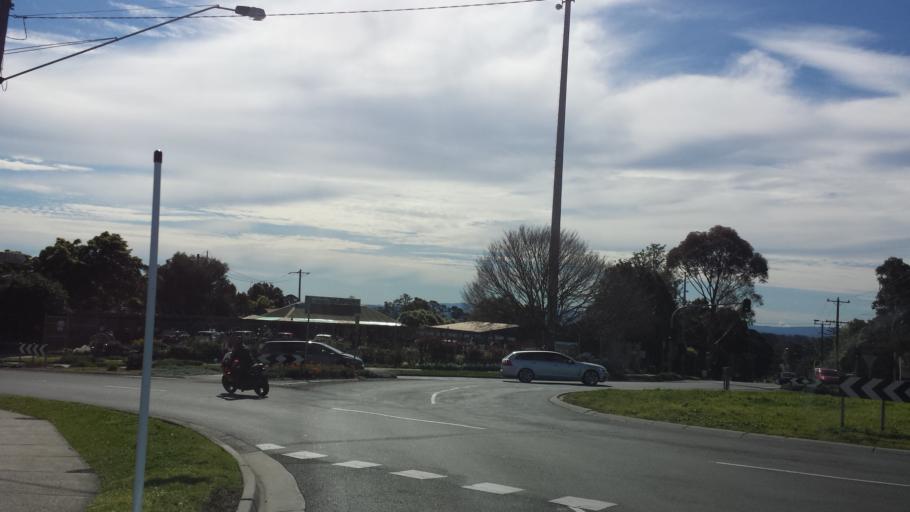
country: AU
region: Victoria
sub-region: Maroondah
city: Warranwood
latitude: -37.7941
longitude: 145.2353
